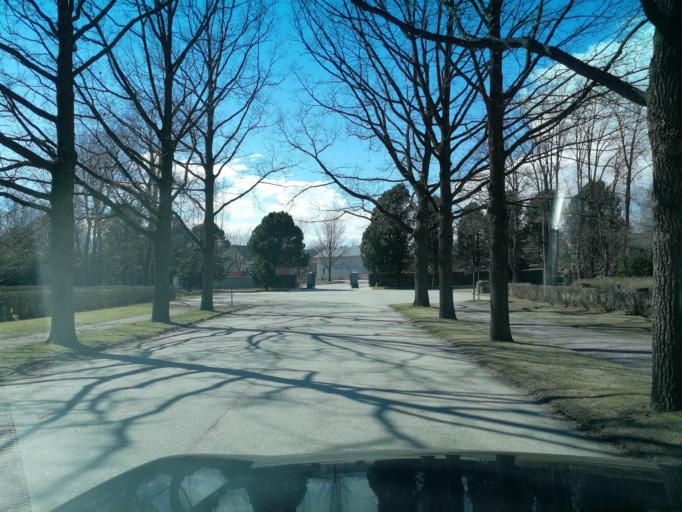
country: FI
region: Uusimaa
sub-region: Helsinki
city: Vantaa
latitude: 60.2338
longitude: 25.0227
